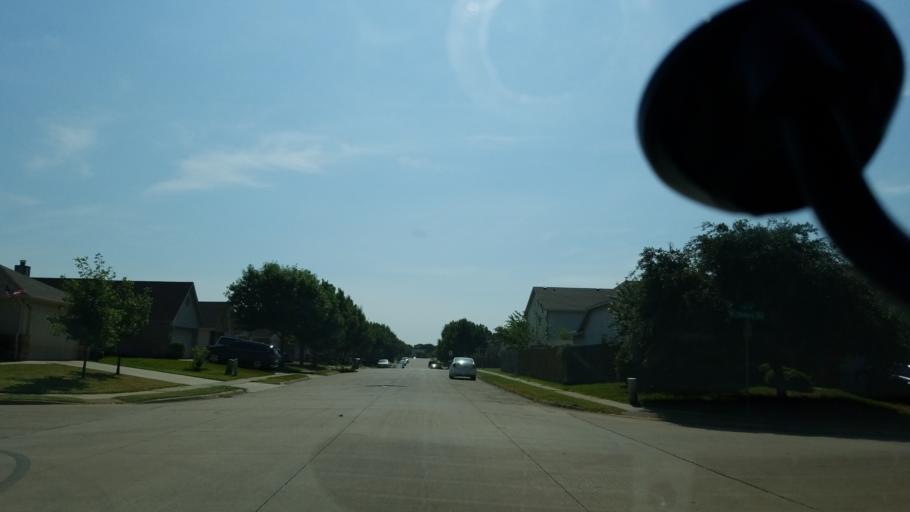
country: US
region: Texas
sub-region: Dallas County
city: Cockrell Hill
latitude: 32.7120
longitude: -96.8722
